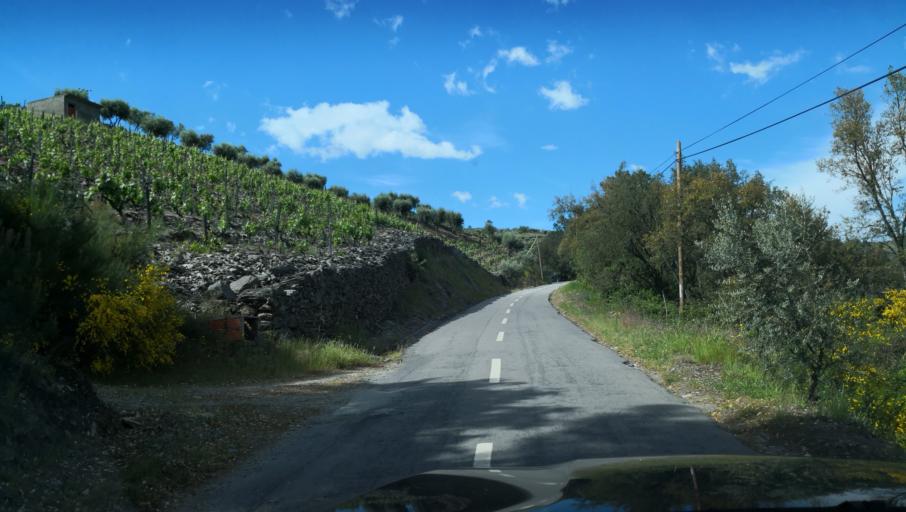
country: PT
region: Vila Real
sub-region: Vila Real
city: Vila Real
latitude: 41.2462
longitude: -7.7379
